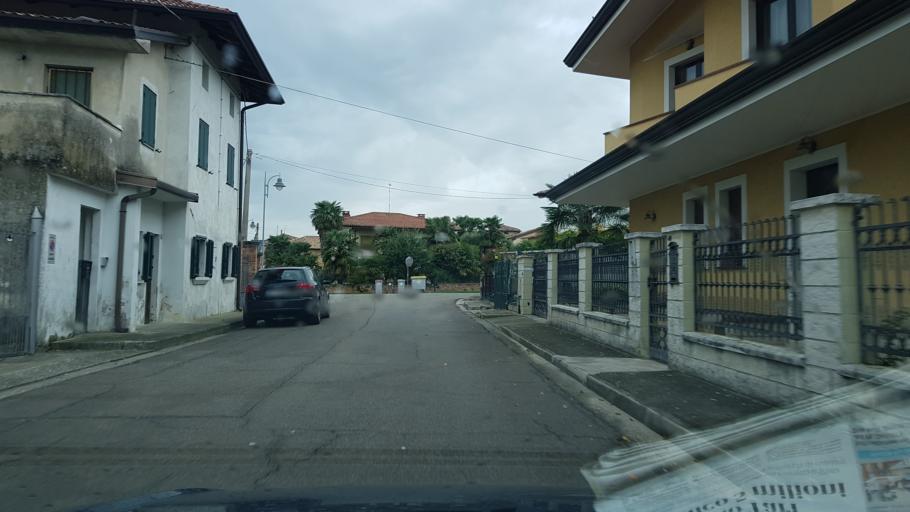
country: IT
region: Friuli Venezia Giulia
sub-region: Provincia di Udine
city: Fiumicello
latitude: 45.8016
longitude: 13.4015
